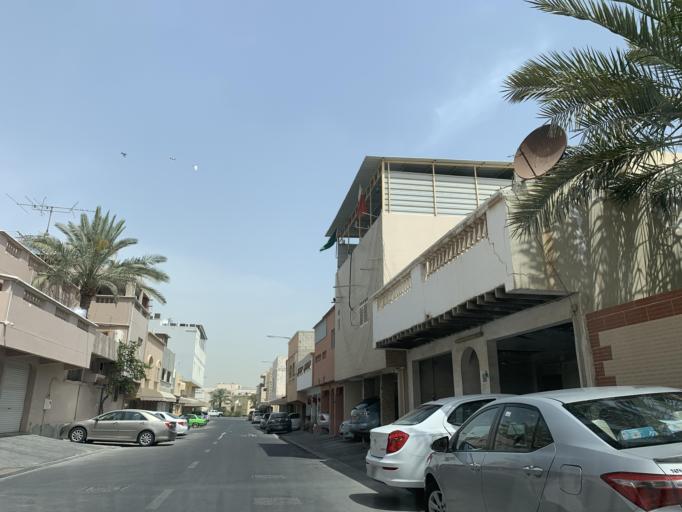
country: BH
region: Northern
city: Madinat `Isa
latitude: 26.1699
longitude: 50.5605
